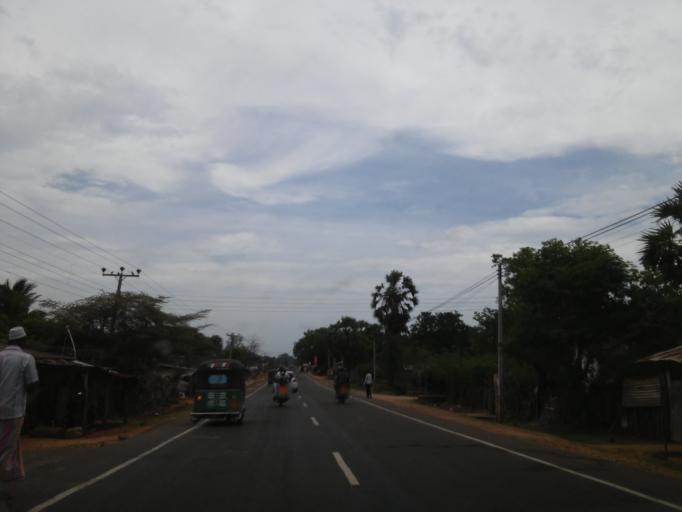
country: LK
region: Eastern Province
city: Trincomalee
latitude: 8.6449
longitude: 81.2022
